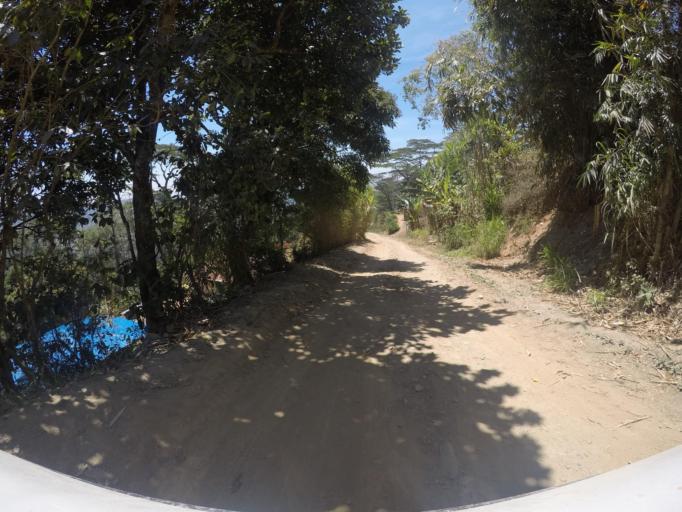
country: TL
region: Ermera
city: Gleno
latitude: -8.7418
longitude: 125.4036
